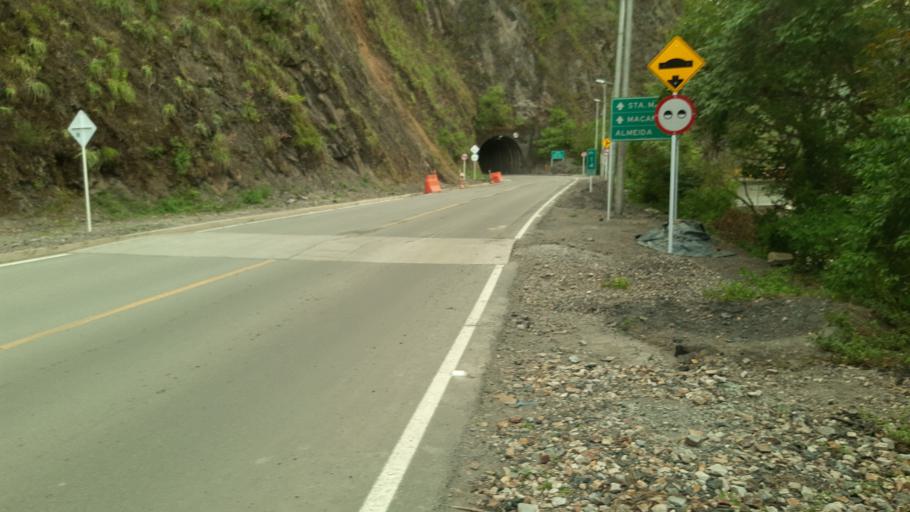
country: CO
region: Boyaca
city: Somondoco
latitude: 5.0167
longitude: -73.3867
